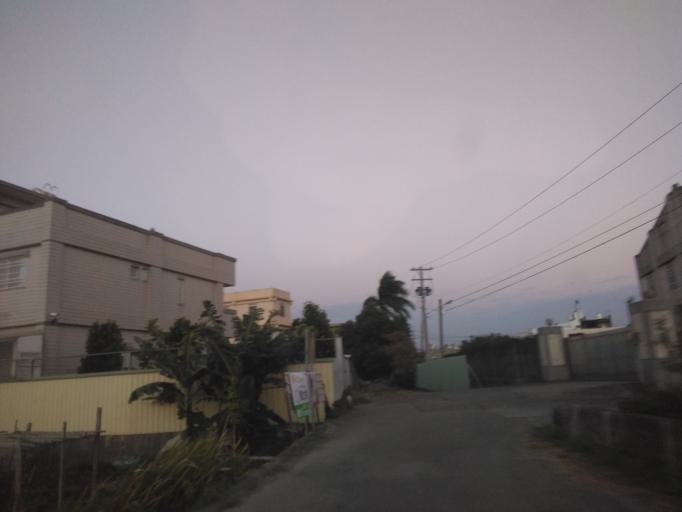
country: TW
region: Taiwan
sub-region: Changhua
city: Chang-hua
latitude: 24.0846
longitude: 120.5982
